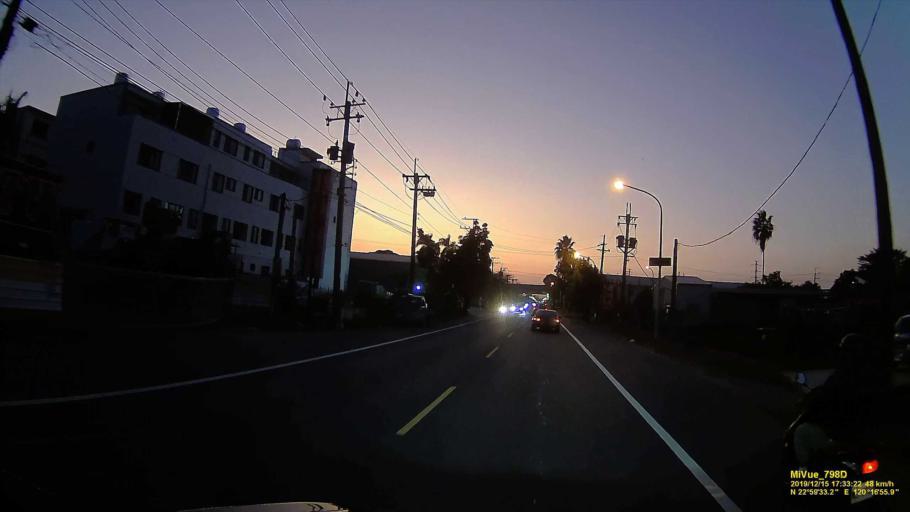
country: TW
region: Taiwan
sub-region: Tainan
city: Tainan
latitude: 22.9925
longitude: 120.2818
